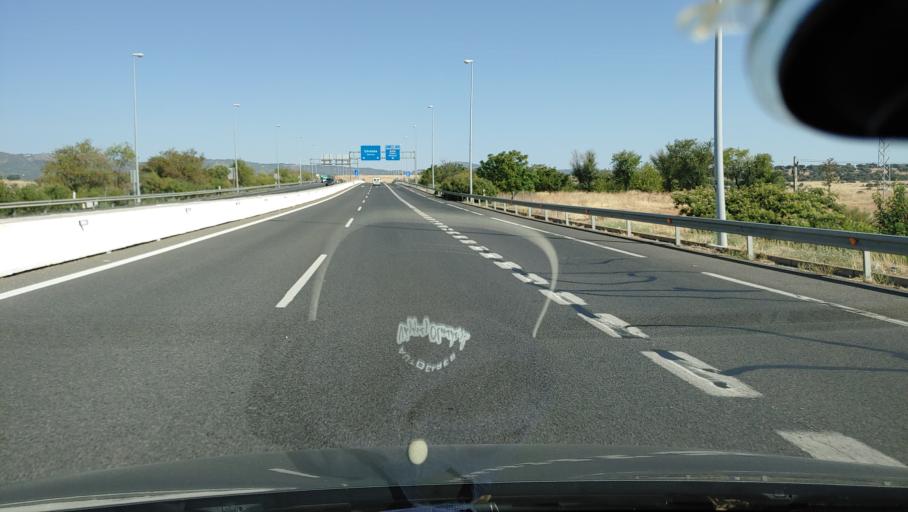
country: ES
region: Andalusia
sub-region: Province of Cordoba
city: Cordoba
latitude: 37.9001
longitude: -4.7489
